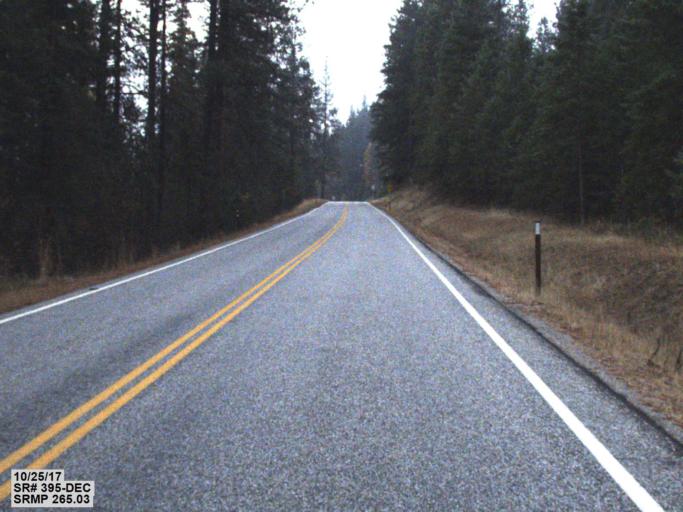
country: CA
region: British Columbia
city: Grand Forks
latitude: 48.9276
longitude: -118.2183
